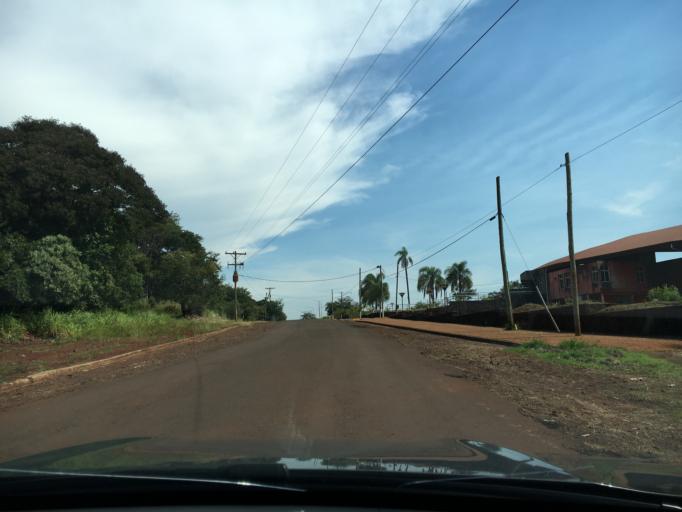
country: AR
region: Misiones
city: Puerto Rico
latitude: -26.8064
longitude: -55.0111
